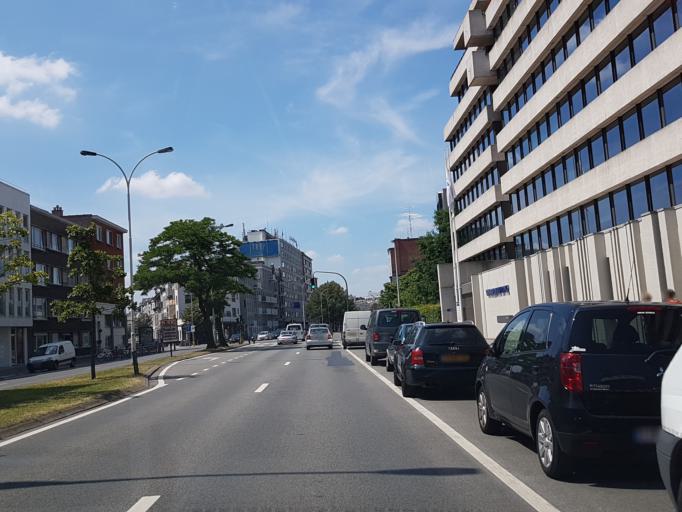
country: BE
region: Flanders
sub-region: Provincie Antwerpen
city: Antwerpen
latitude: 51.2091
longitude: 4.4336
